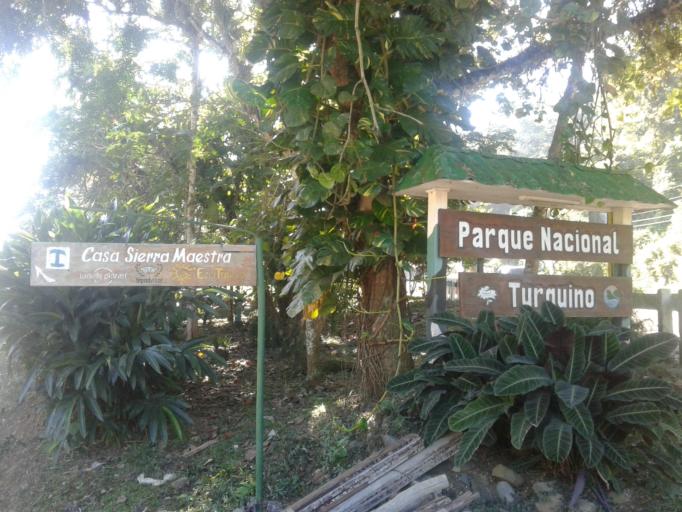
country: CU
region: Granma
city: Bartolome Maso
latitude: 20.0424
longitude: -76.9047
